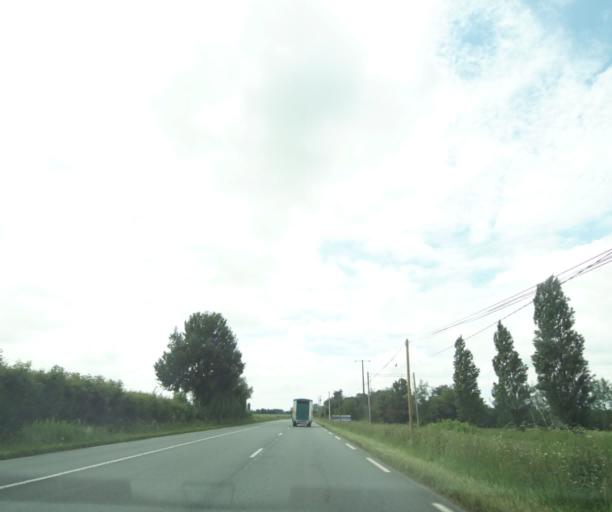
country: FR
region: Poitou-Charentes
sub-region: Departement des Deux-Sevres
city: Champdeniers-Saint-Denis
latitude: 46.5043
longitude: -0.3371
